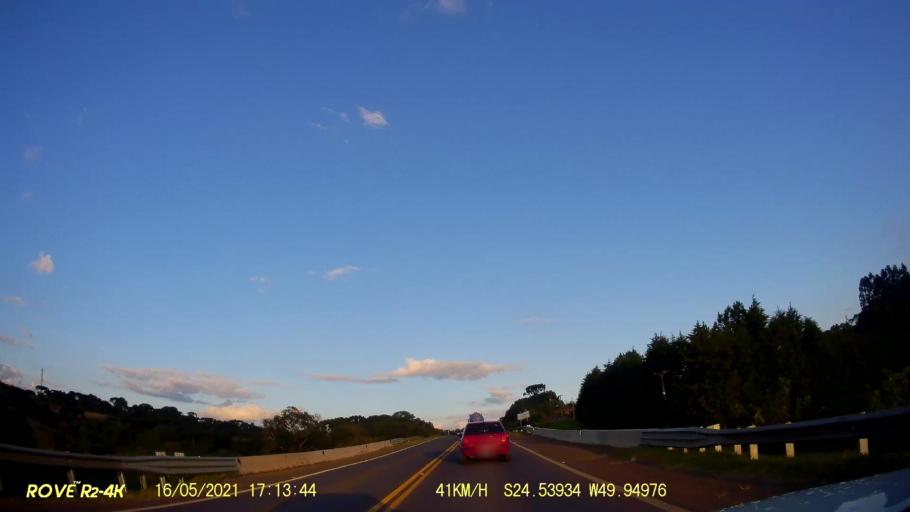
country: BR
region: Parana
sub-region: Pirai Do Sul
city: Pirai do Sul
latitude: -24.5398
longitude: -49.9499
